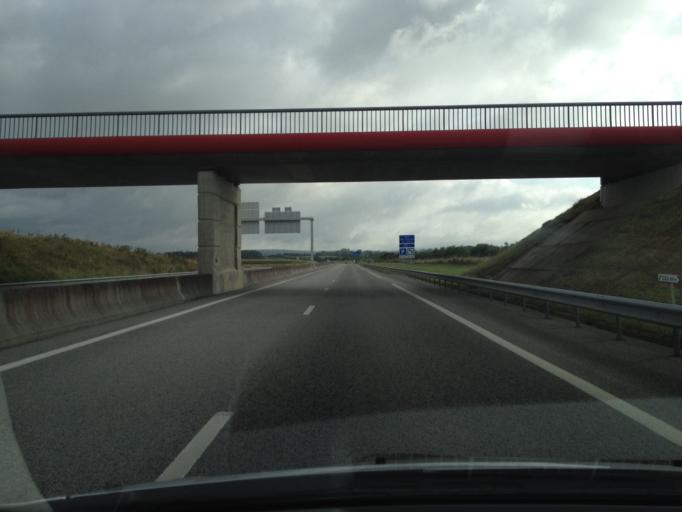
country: FR
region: Lower Normandy
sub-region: Departement de l'Orne
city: Sees
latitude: 48.6393
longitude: 0.2077
